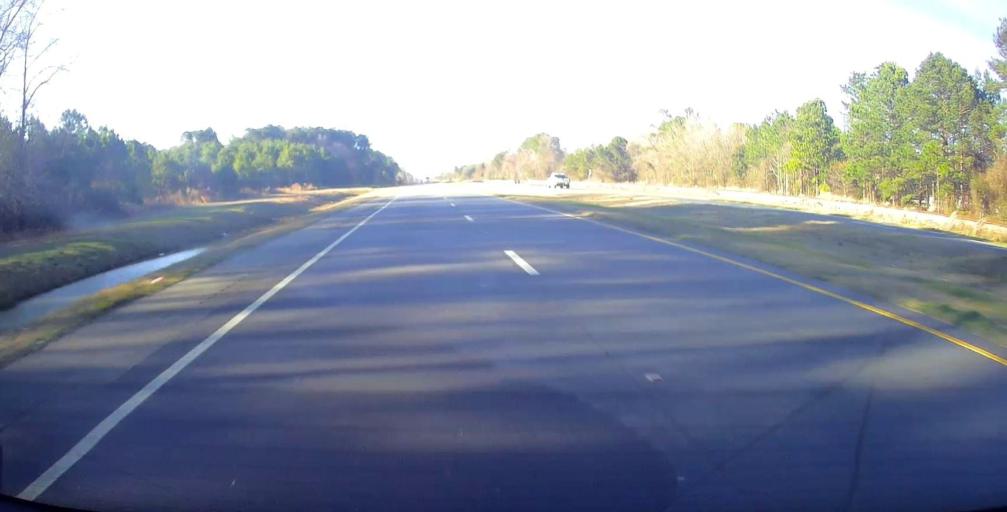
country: US
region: Georgia
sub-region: Lee County
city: Leesburg
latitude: 31.8348
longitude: -84.2209
